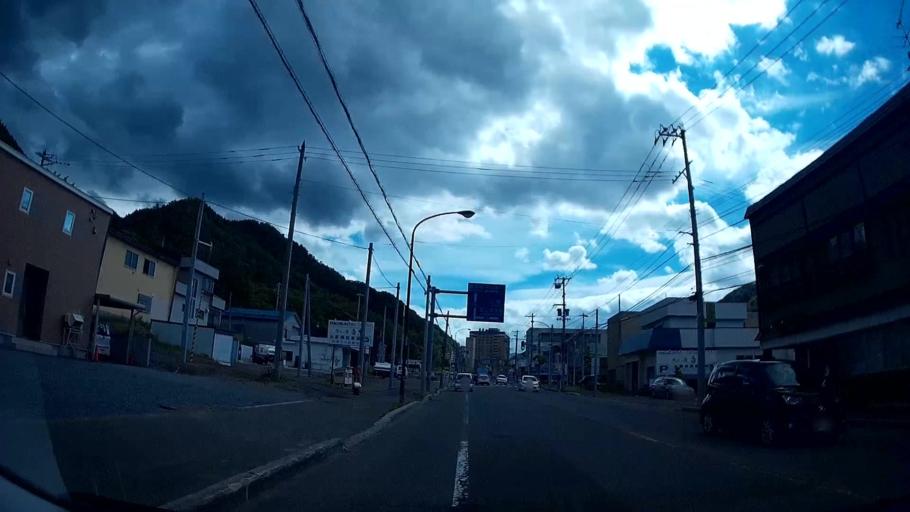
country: JP
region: Hokkaido
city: Sapporo
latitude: 42.9678
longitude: 141.1689
